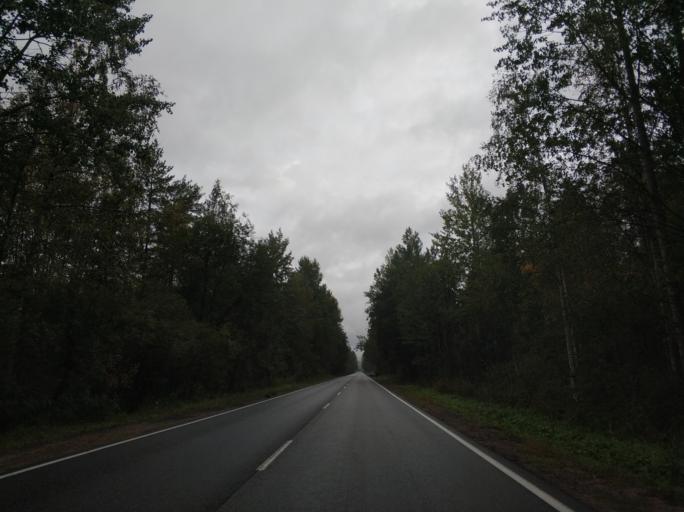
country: RU
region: Leningrad
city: Borisova Griva
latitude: 60.1514
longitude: 30.9363
